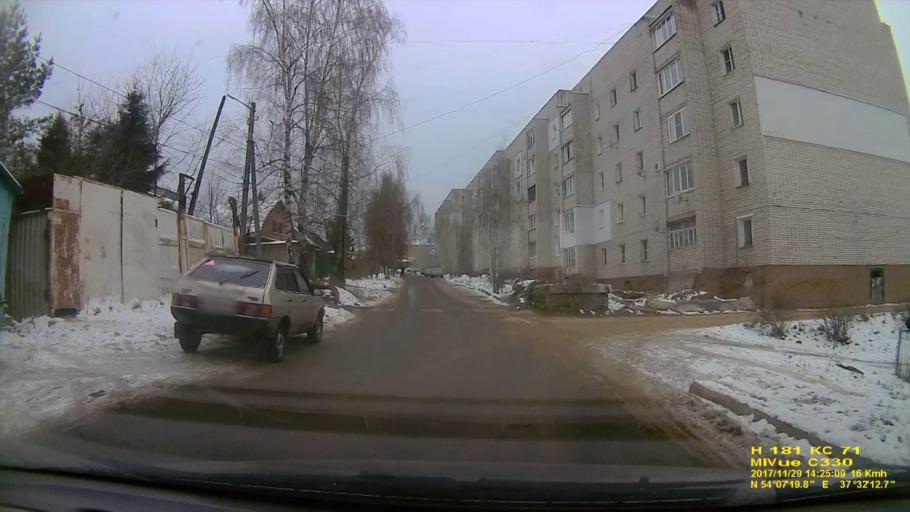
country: RU
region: Tula
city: Kosaya Gora
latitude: 54.1222
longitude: 37.5369
